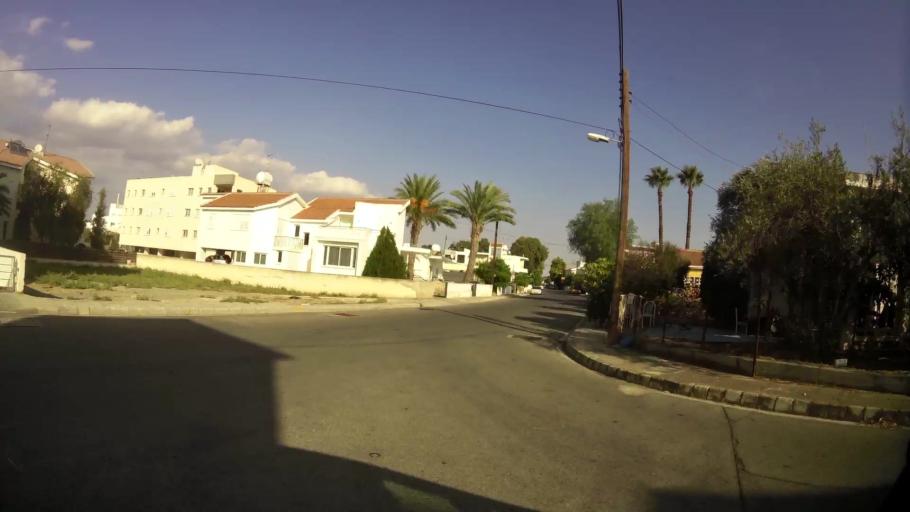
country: CY
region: Lefkosia
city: Nicosia
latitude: 35.1775
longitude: 33.3217
